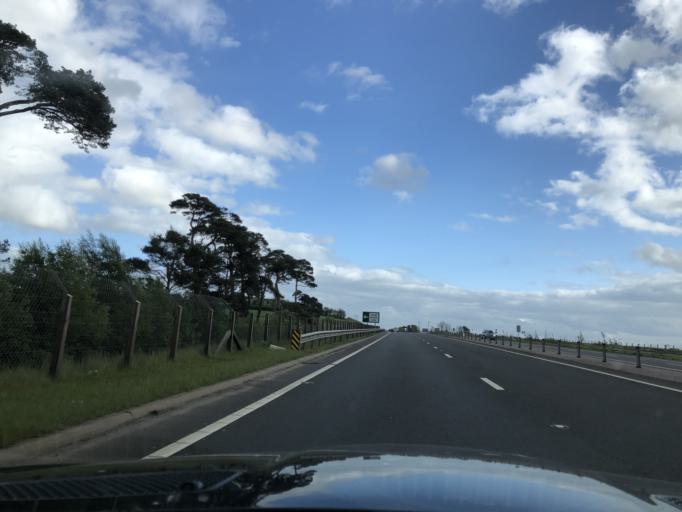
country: GB
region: Northern Ireland
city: Dunloy
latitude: 54.9818
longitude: -6.3476
